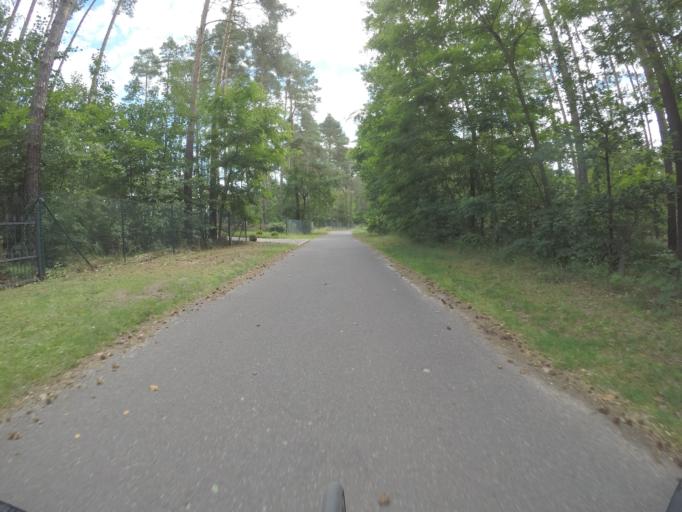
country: DE
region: Brandenburg
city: Reichenwalde
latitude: 52.2303
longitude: 13.9753
